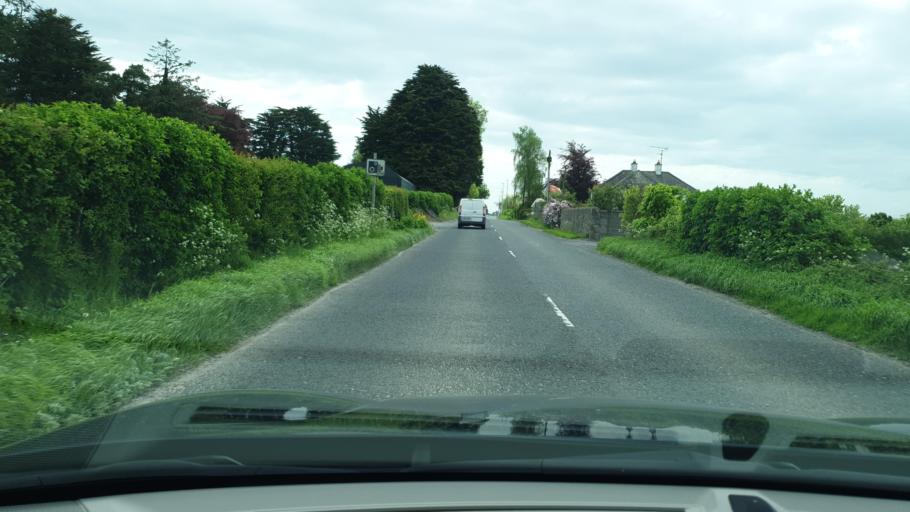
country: IE
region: Leinster
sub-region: An Mhi
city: Navan
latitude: 53.7100
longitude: -6.6891
